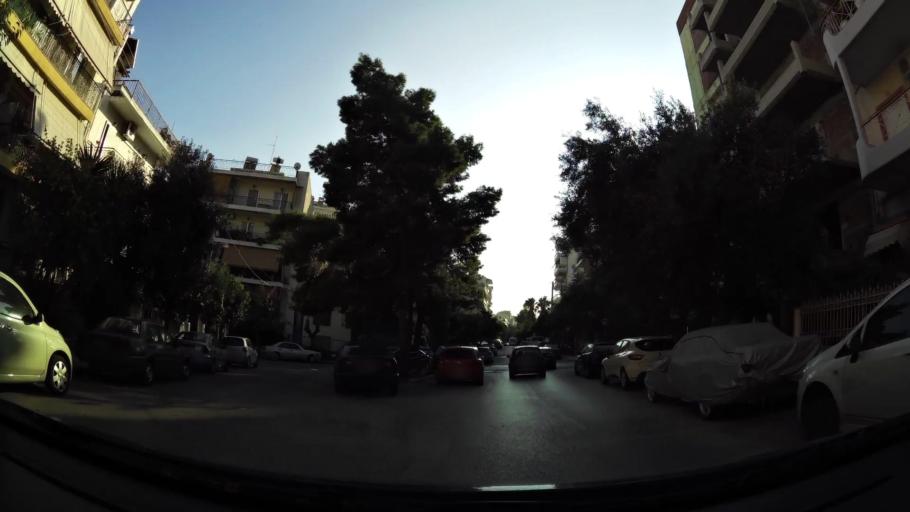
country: GR
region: Attica
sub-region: Nomos Piraios
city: Nikaia
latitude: 37.9703
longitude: 23.6374
